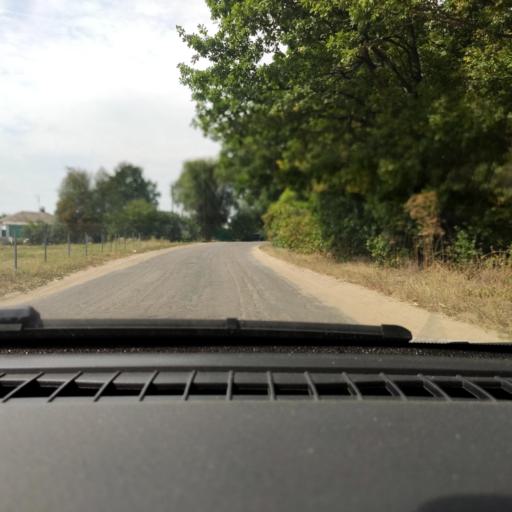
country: RU
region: Voronezj
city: Pridonskoy
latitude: 51.7384
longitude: 39.0569
